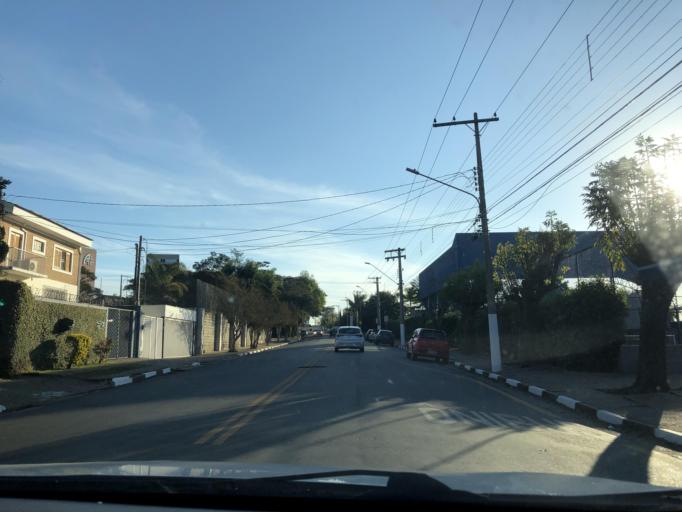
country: BR
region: Sao Paulo
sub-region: Atibaia
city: Atibaia
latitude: -23.1152
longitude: -46.5411
